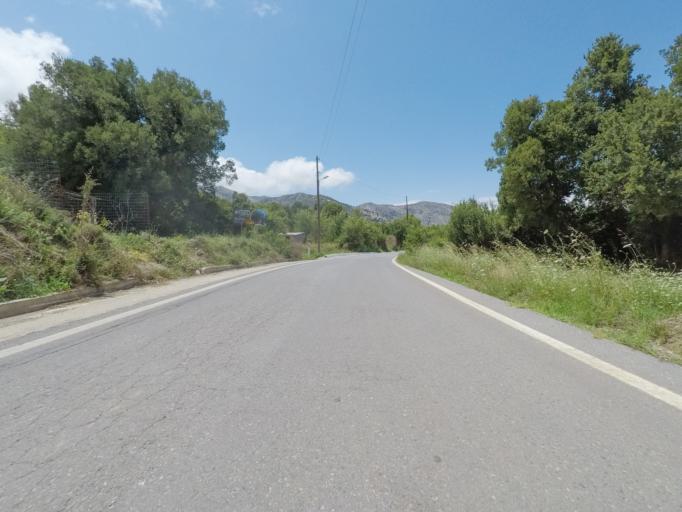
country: GR
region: Crete
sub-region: Nomos Irakleiou
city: Mokhos
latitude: 35.1683
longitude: 25.4468
